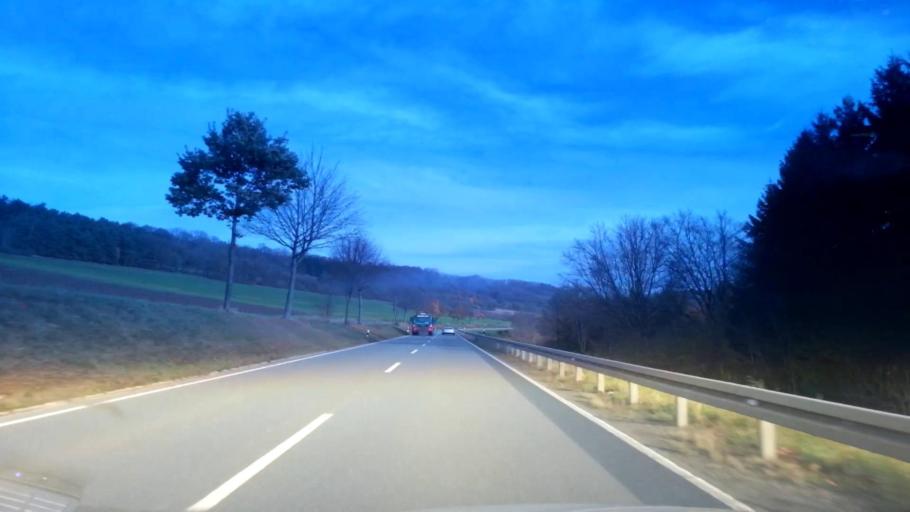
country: DE
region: Bavaria
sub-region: Upper Franconia
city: Reuth
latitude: 49.9666
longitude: 11.6627
